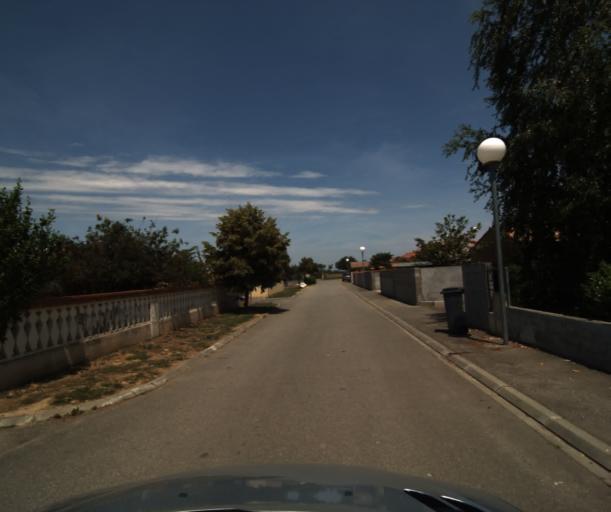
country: FR
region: Midi-Pyrenees
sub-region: Departement de la Haute-Garonne
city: Labastidette
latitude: 43.4636
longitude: 1.2521
